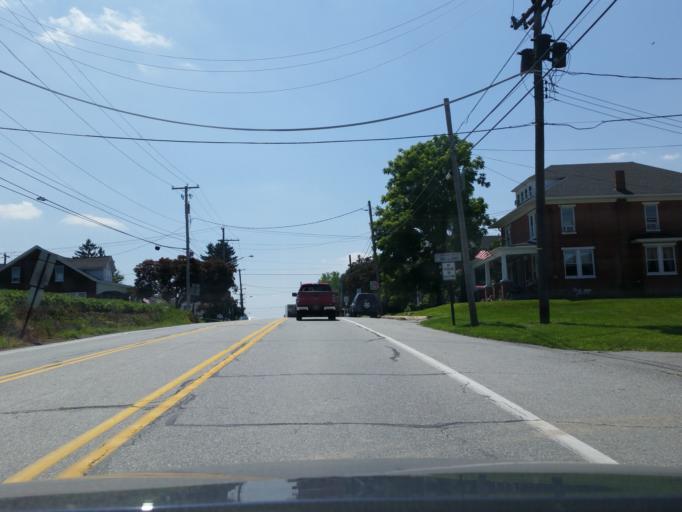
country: US
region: Pennsylvania
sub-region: York County
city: Hallam
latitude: 40.0086
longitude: -76.5952
